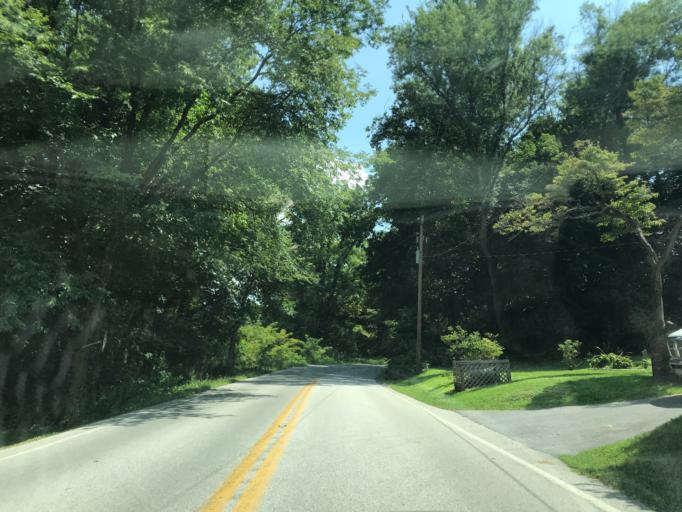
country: US
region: Pennsylvania
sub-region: York County
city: New Freedom
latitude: 39.7291
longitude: -76.7335
